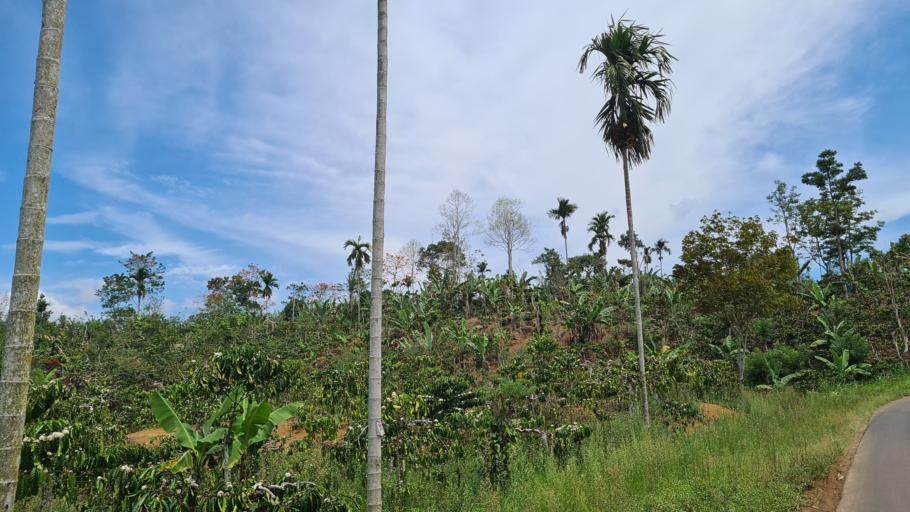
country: ID
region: Lampung
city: Kenali
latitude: -5.0964
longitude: 104.4287
